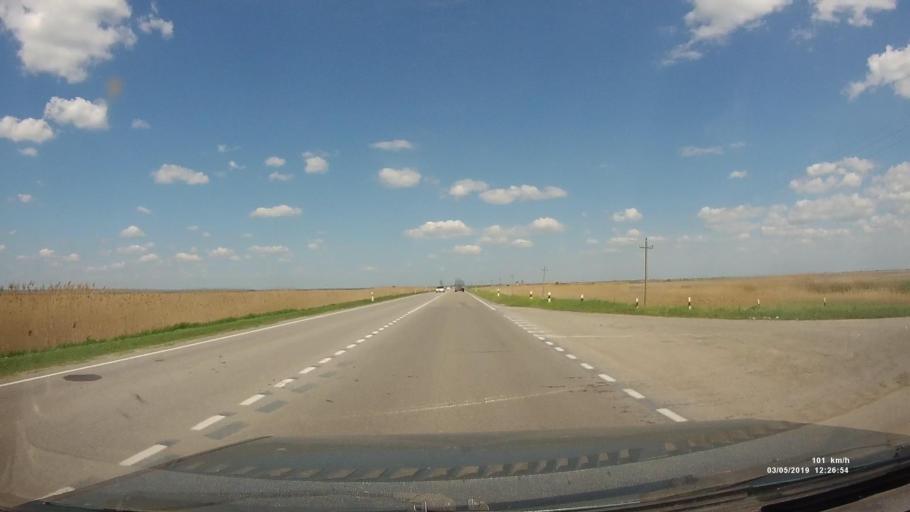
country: RU
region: Rostov
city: Semikarakorsk
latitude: 47.4520
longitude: 40.7172
